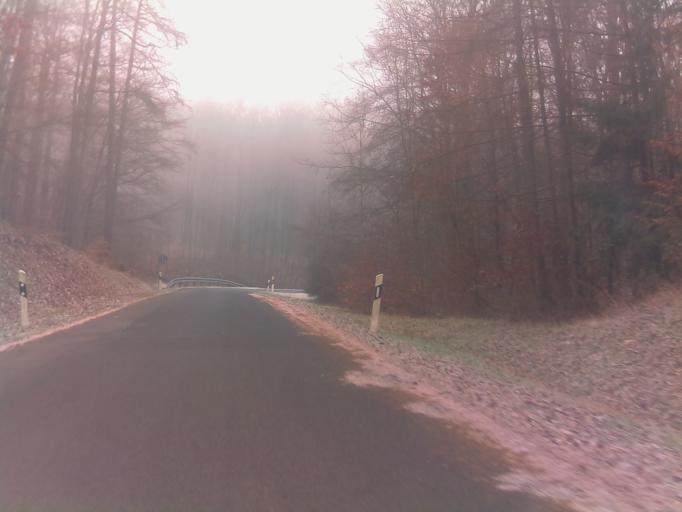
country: DE
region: Bavaria
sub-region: Regierungsbezirk Unterfranken
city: Burgpreppach
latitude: 50.1017
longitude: 10.6006
